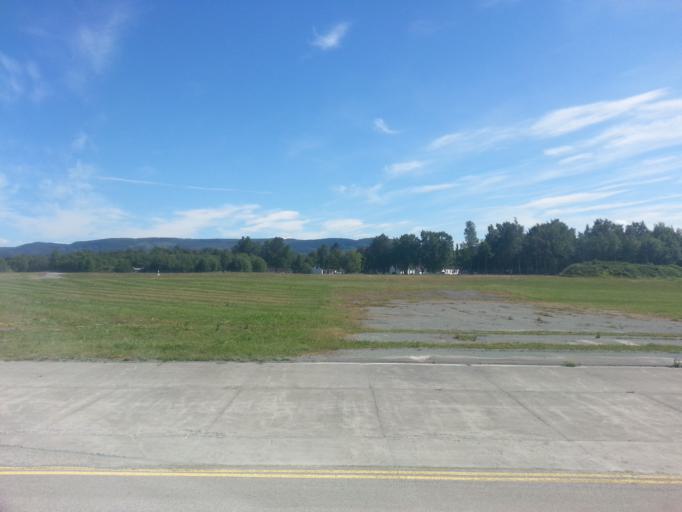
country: NO
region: Nord-Trondelag
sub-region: Stjordal
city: Stjordalshalsen
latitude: 63.4572
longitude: 10.9411
